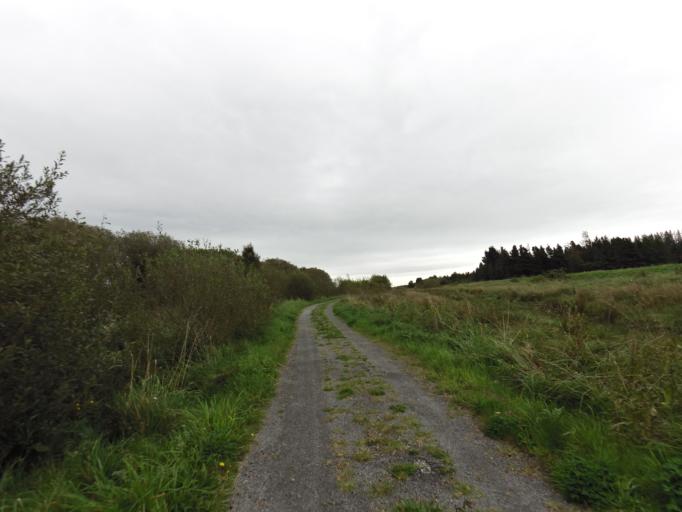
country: IE
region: Leinster
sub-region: Uibh Fhaili
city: Ferbane
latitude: 53.2537
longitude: -7.7471
